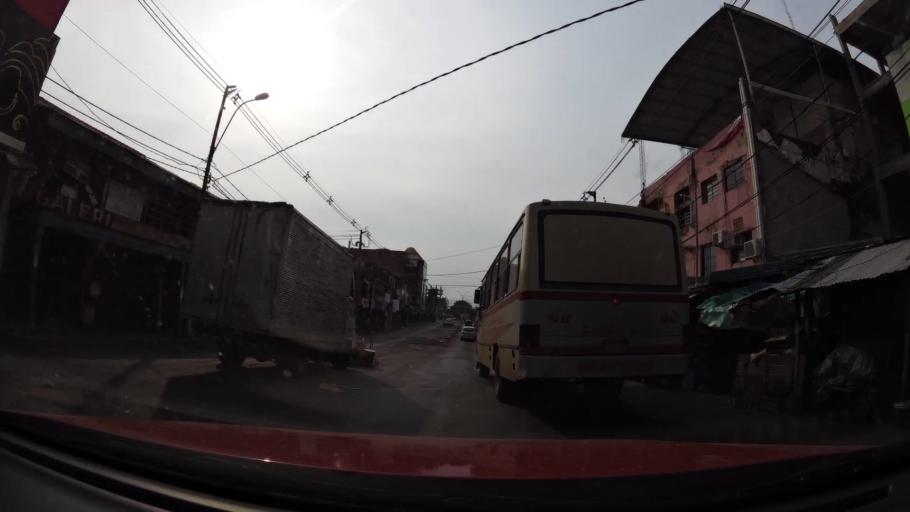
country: PY
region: Asuncion
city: Asuncion
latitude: -25.2994
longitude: -57.6245
